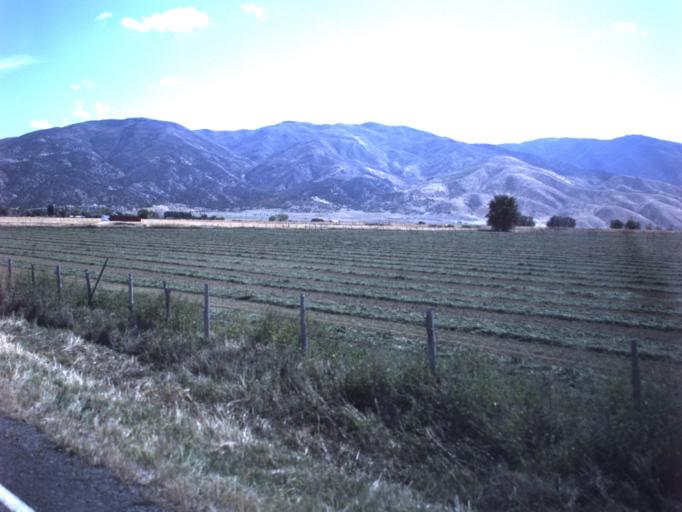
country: US
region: Utah
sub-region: Juab County
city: Nephi
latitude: 39.5581
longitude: -111.8884
